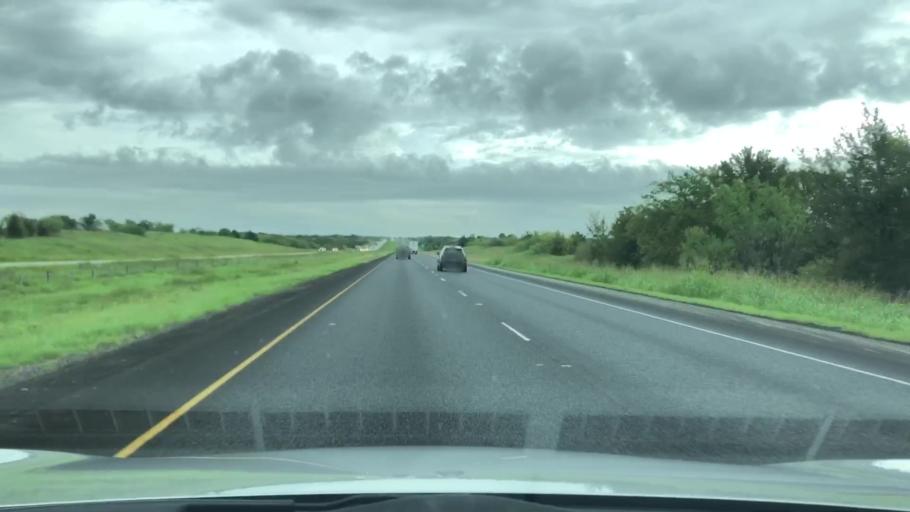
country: US
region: Texas
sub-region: Gonzales County
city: Waelder
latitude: 29.6667
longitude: -97.3310
